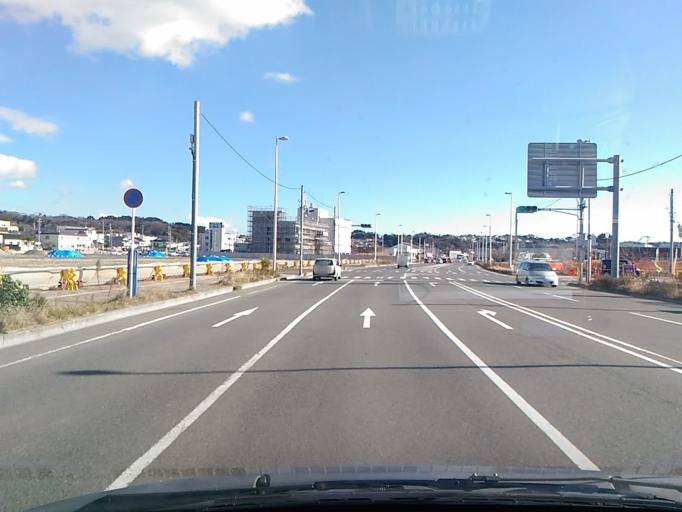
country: JP
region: Fukushima
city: Iwaki
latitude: 36.9462
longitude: 140.9040
